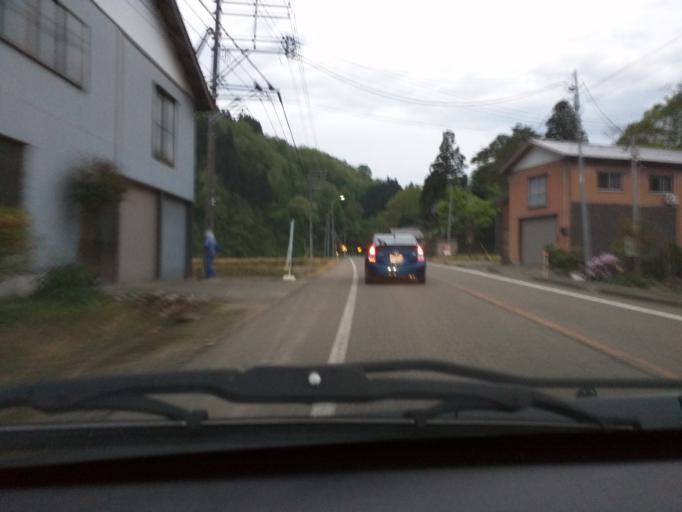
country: JP
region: Niigata
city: Ojiya
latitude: 37.3199
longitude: 138.7040
